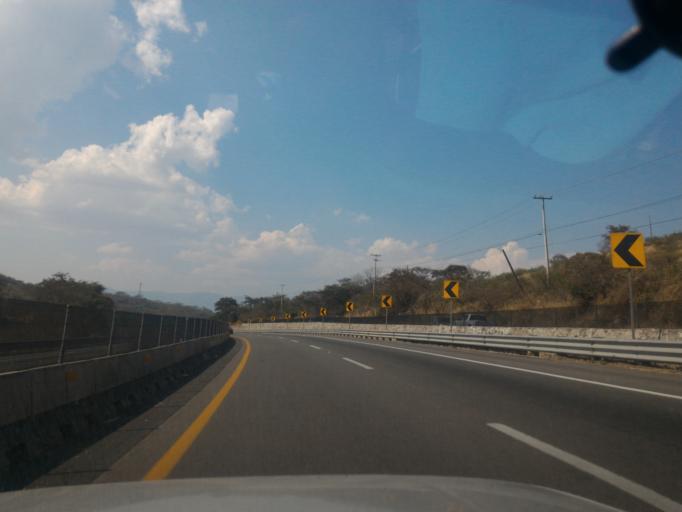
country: MX
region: Jalisco
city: San Andres Ixtlan
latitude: 19.8413
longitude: -103.5016
